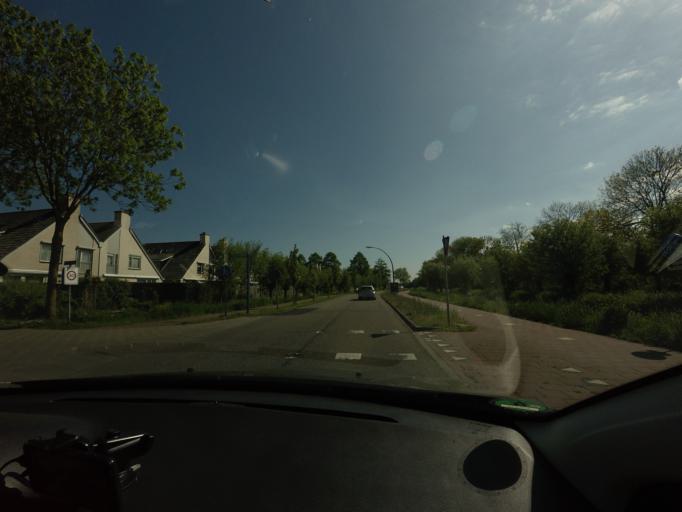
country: NL
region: Utrecht
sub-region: Gemeente De Ronde Venen
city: Mijdrecht
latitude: 52.2085
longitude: 4.9198
